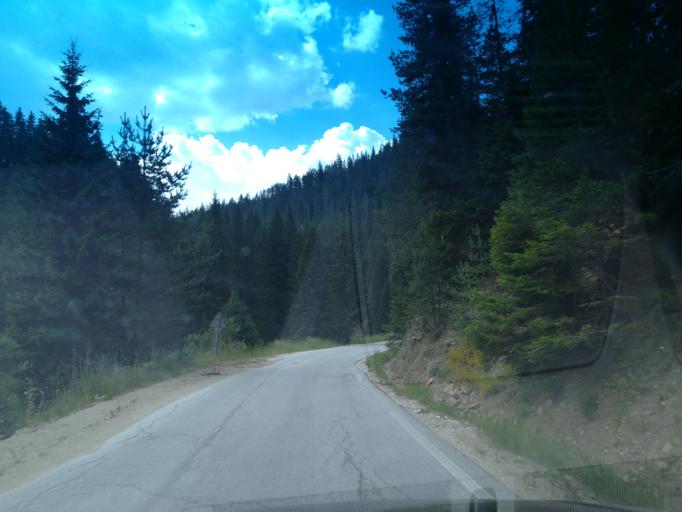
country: BG
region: Smolyan
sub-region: Obshtina Chepelare
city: Chepelare
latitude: 41.6624
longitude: 24.6617
